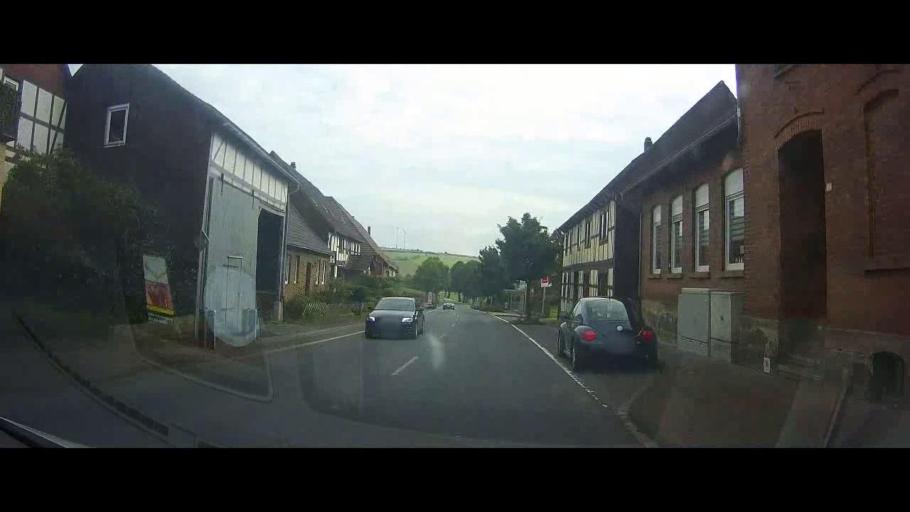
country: DE
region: Lower Saxony
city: Uslar
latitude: 51.6507
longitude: 9.6515
